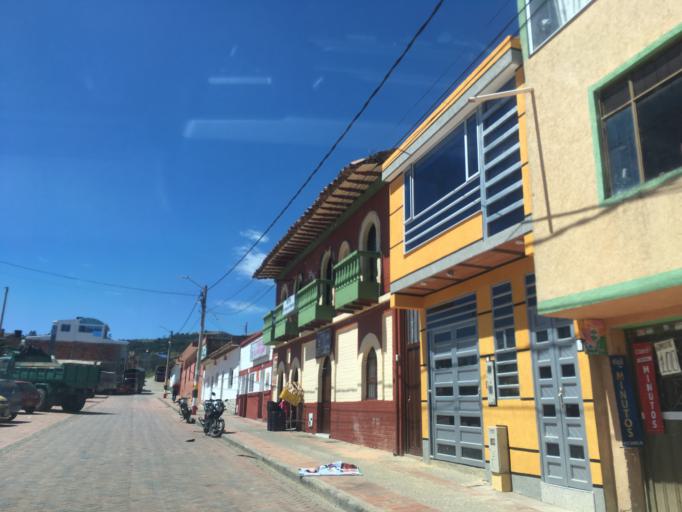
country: CO
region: Boyaca
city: Combita
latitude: 5.6341
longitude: -73.3241
